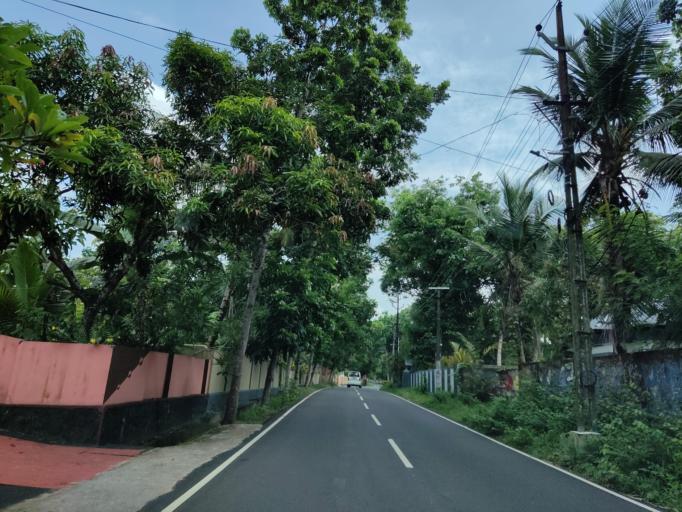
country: IN
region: Kerala
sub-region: Alappuzha
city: Mavelikara
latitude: 9.2649
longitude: 76.5593
